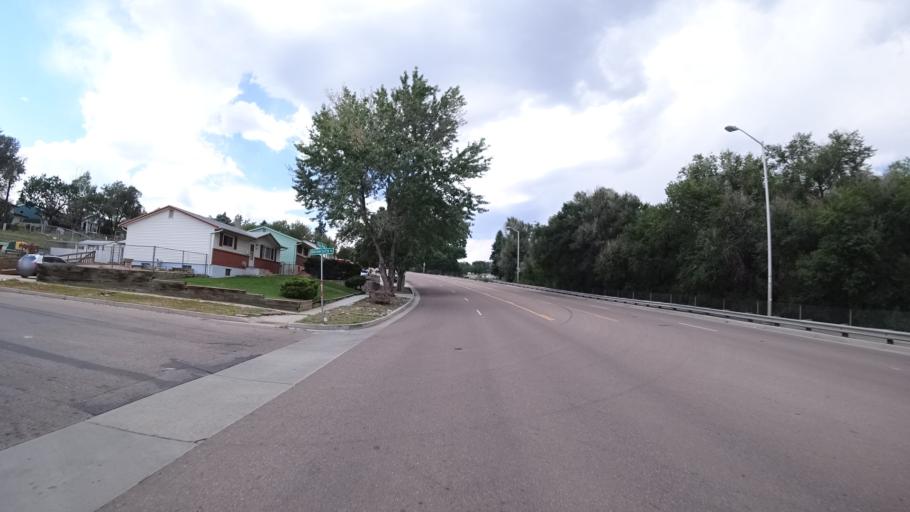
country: US
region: Colorado
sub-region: El Paso County
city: Colorado Springs
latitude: 38.8323
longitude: -104.7625
